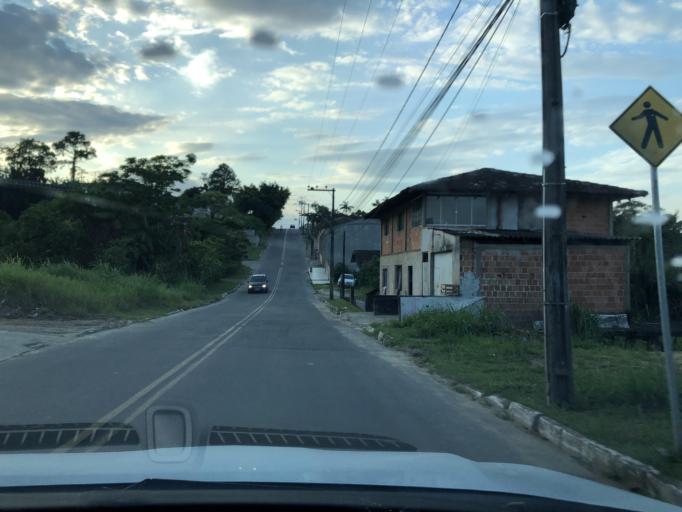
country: BR
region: Santa Catarina
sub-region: Sao Francisco Do Sul
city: Sao Francisco do Sul
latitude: -26.2508
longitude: -48.6318
